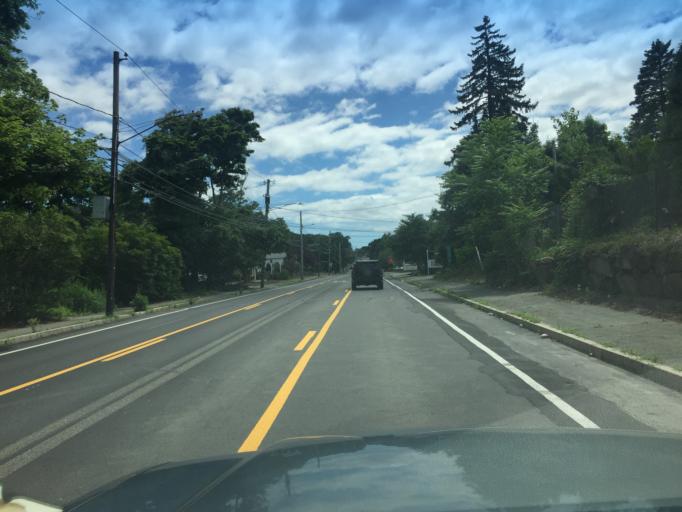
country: US
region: Massachusetts
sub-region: Middlesex County
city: Reading
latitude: 42.5145
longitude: -71.1038
